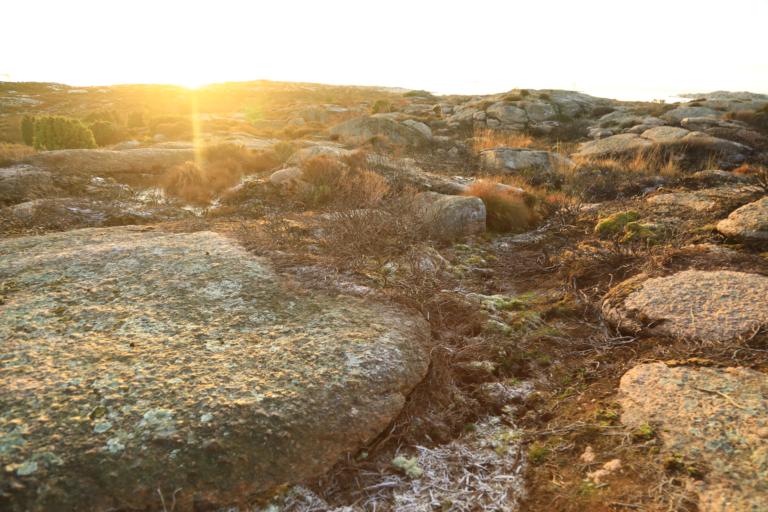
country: SE
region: Halland
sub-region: Varbergs Kommun
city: Varberg
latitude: 57.1913
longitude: 12.1619
